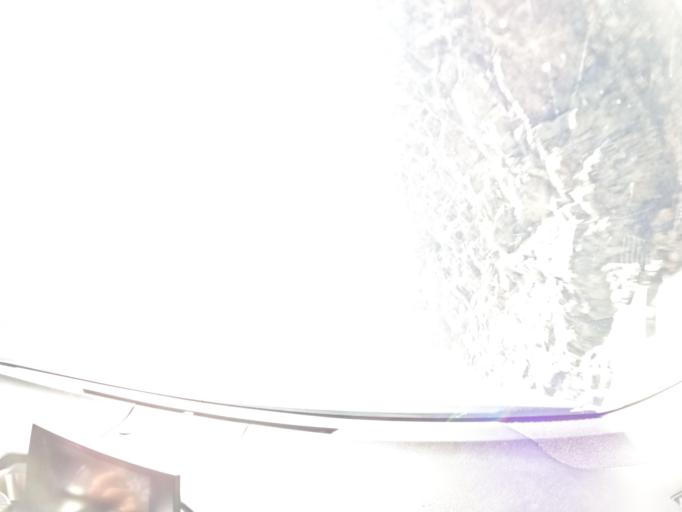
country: TW
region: Taiwan
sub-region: Taitung
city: Taitung
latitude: 23.1751
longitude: 121.0345
